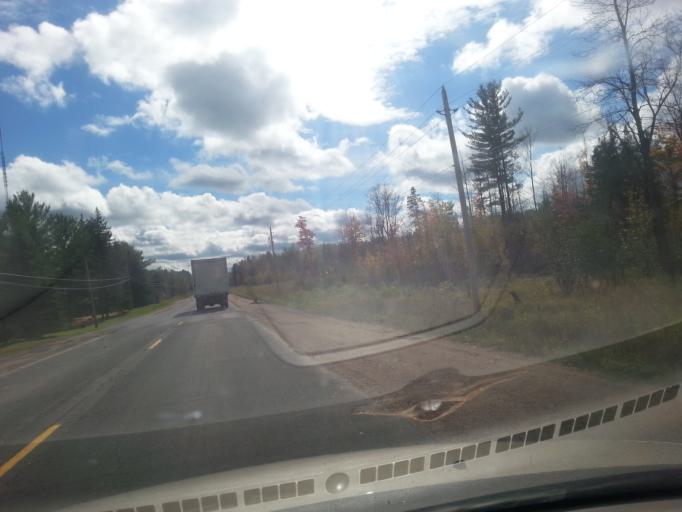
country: CA
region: Ontario
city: Pembroke
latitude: 45.6855
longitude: -77.1006
